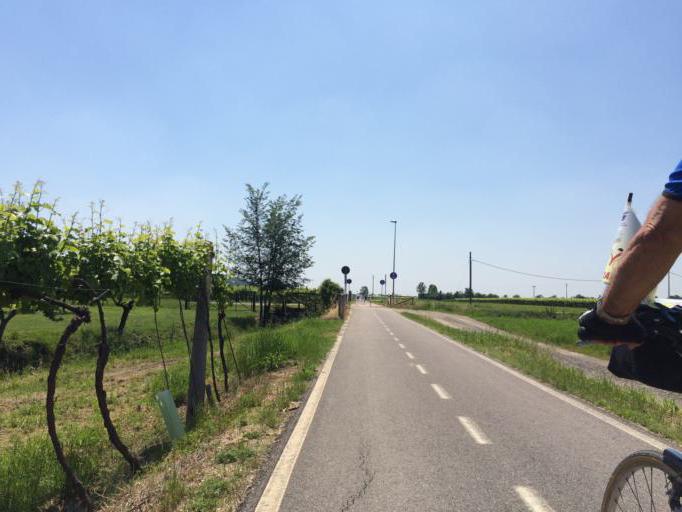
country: IT
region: Veneto
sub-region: Provincia di Vicenza
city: Ponte di Barbarano
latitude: 45.3916
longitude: 11.5630
